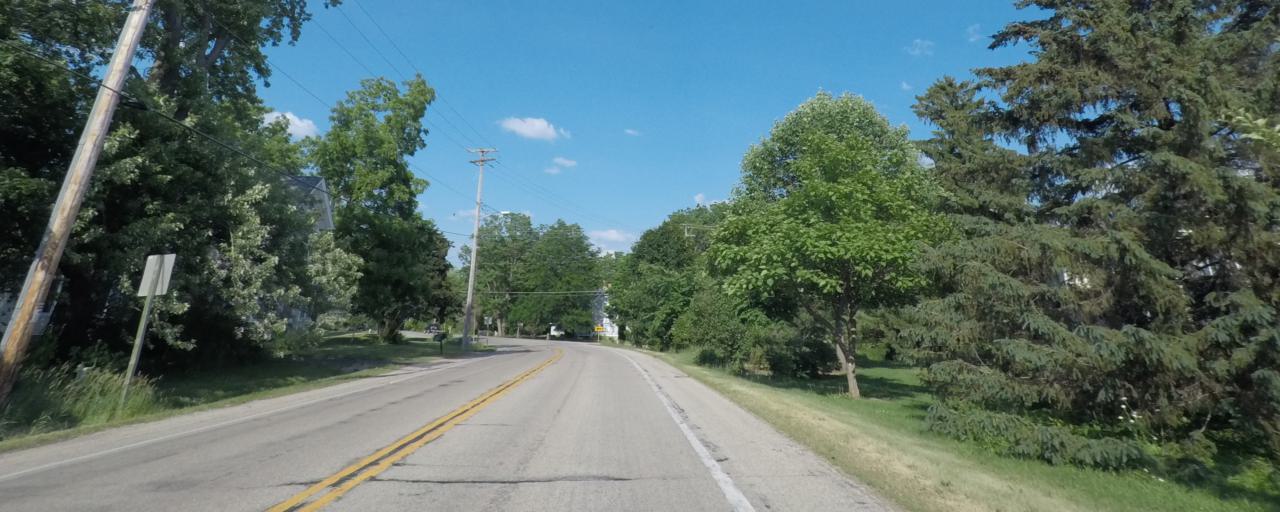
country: US
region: Wisconsin
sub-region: Waukesha County
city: Mukwonago
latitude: 42.8350
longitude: -88.2783
